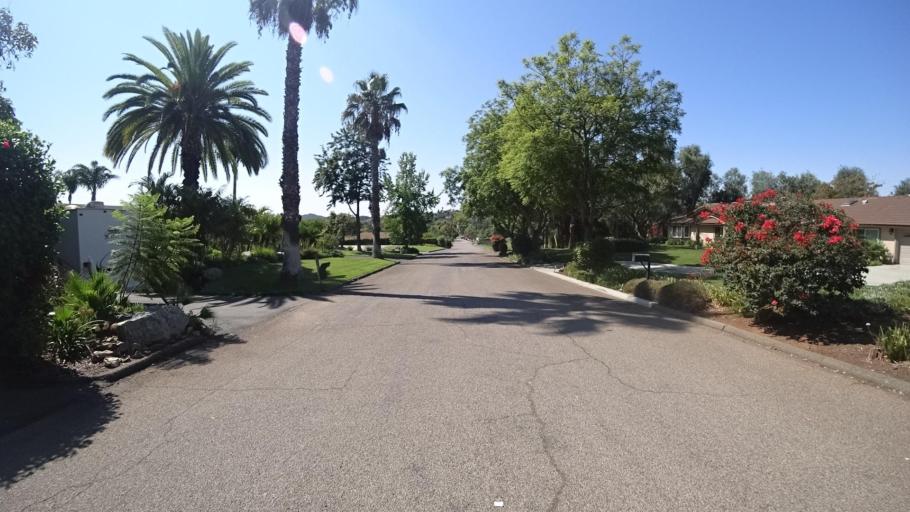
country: US
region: California
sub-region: San Diego County
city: Escondido
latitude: 33.0961
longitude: -117.0945
